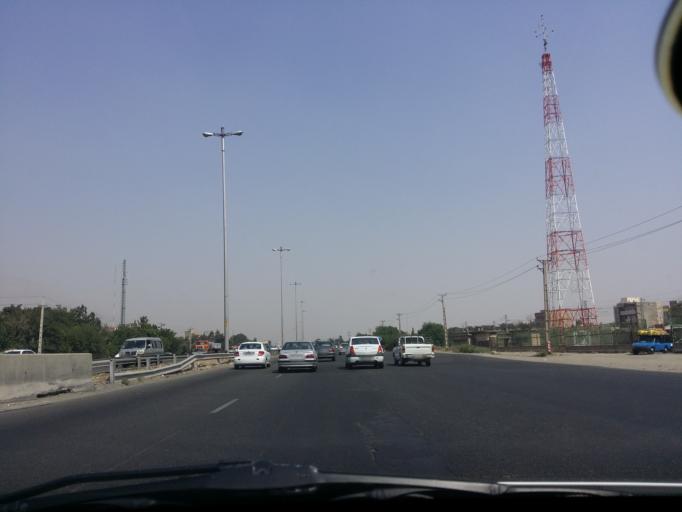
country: IR
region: Alborz
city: Karaj
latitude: 35.7957
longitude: 50.9790
